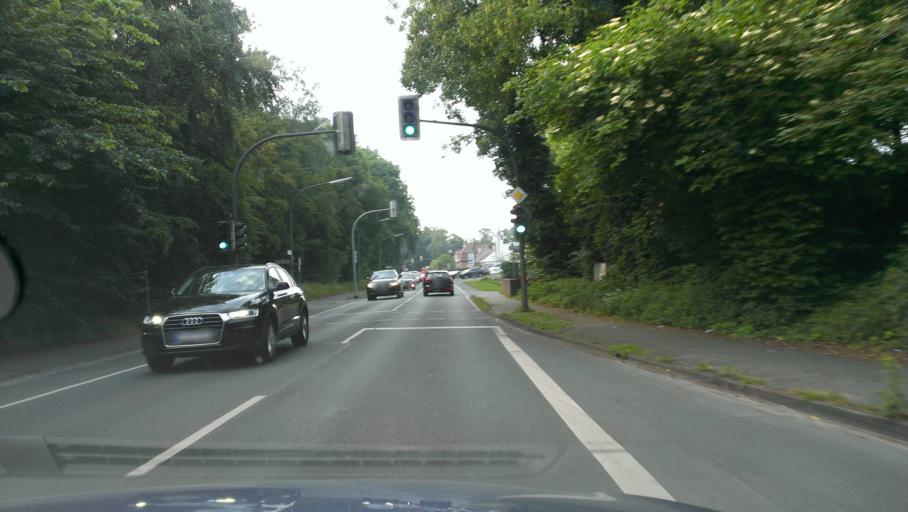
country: DE
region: North Rhine-Westphalia
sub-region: Regierungsbezirk Munster
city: Muenster
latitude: 51.9156
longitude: 7.6815
